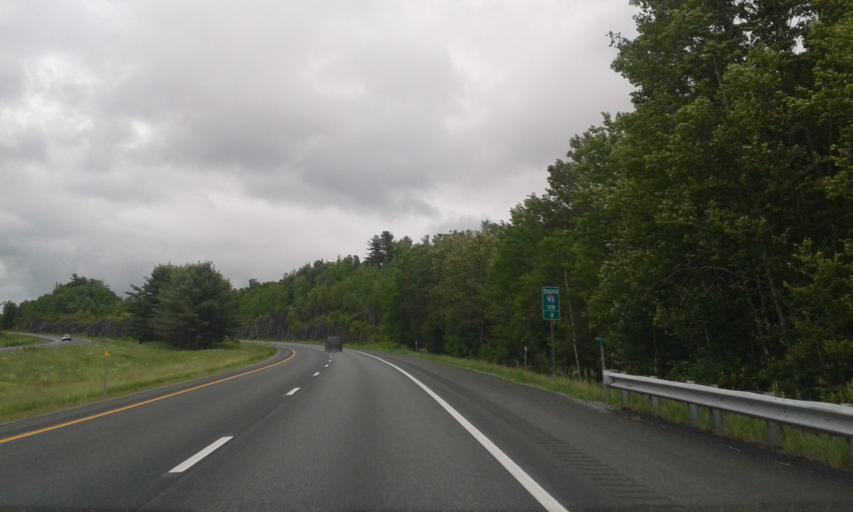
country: US
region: New Hampshire
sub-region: Grafton County
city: Littleton
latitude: 44.3136
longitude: -71.8546
